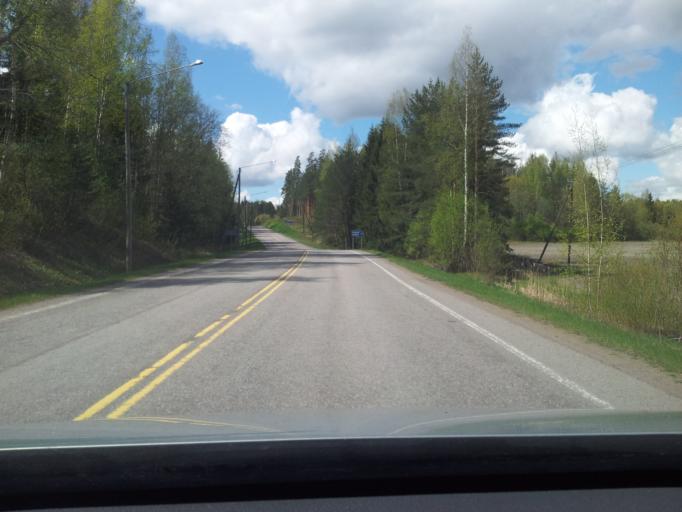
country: FI
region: Uusimaa
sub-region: Loviisa
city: Perna
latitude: 60.5036
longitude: 25.9385
